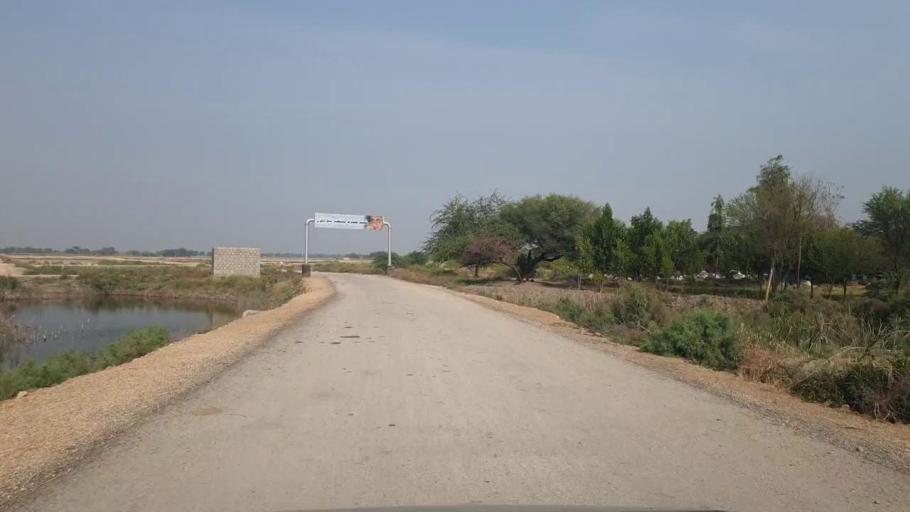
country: PK
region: Sindh
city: Tando Muhammad Khan
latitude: 25.1313
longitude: 68.5204
